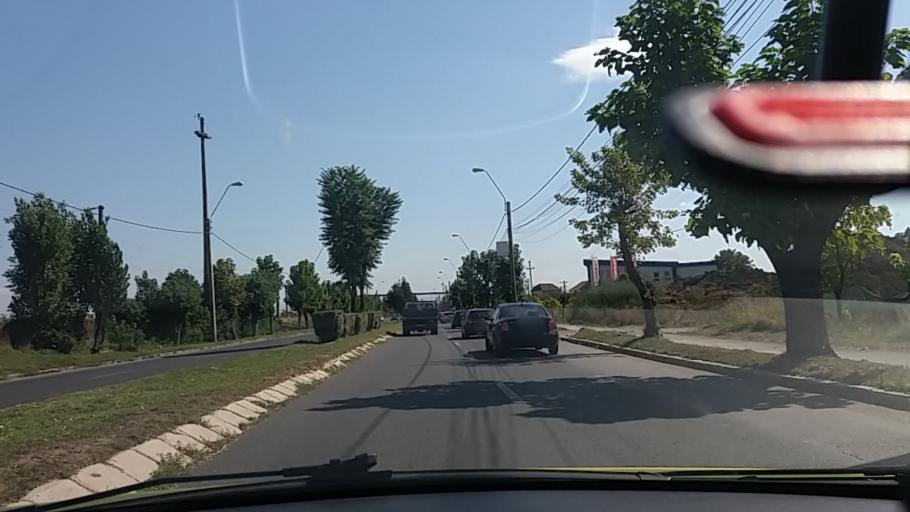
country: RO
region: Hunedoara
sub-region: Municipiul Deva
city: Deva
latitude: 45.8966
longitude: 22.8959
